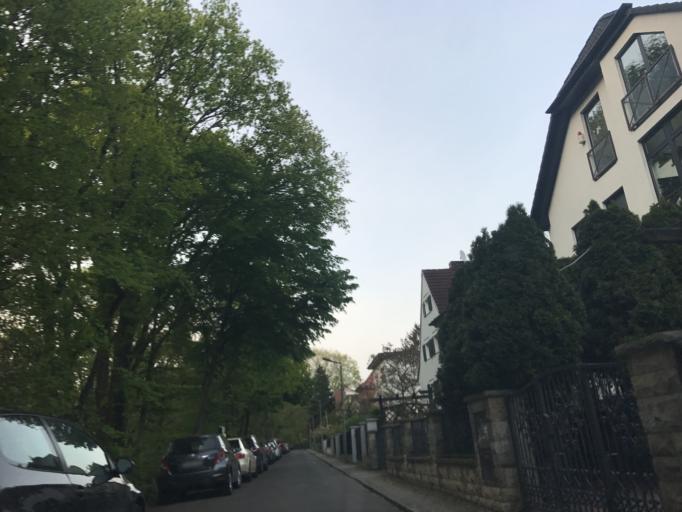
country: DE
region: Berlin
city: Grunewald
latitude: 52.4942
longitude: 13.2601
